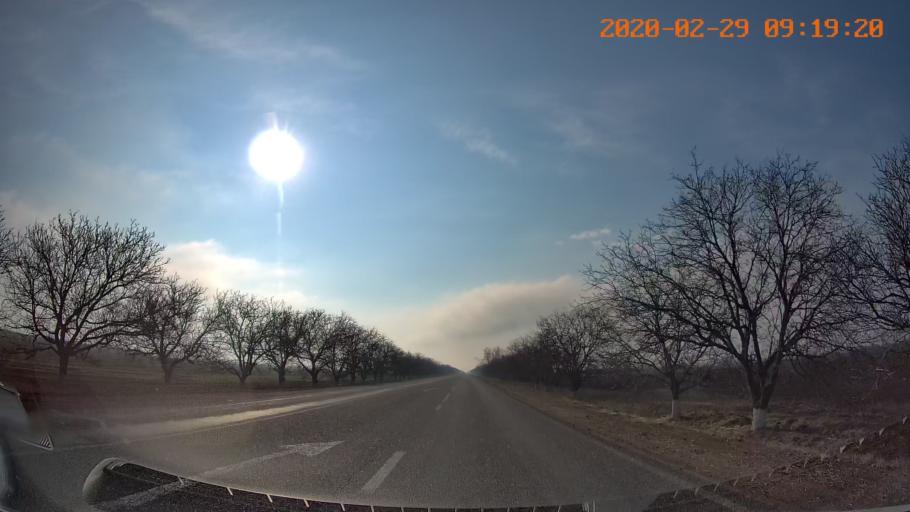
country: MD
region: Telenesti
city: Pervomaisc
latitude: 46.7642
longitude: 29.9380
